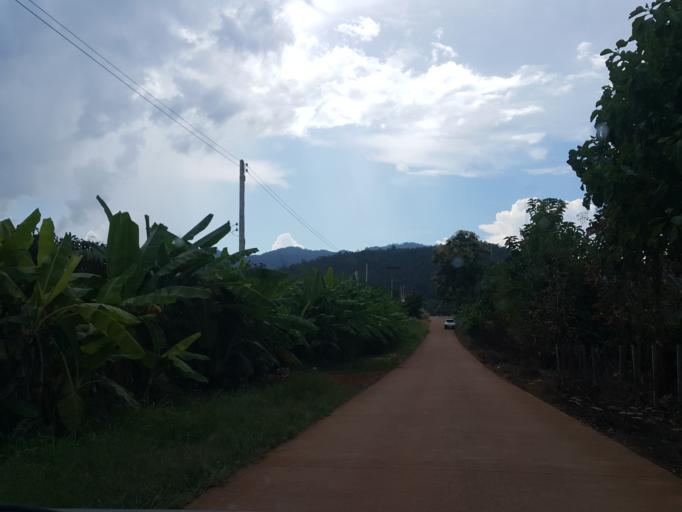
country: TH
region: Chiang Mai
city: Phrao
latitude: 19.3333
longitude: 99.1538
